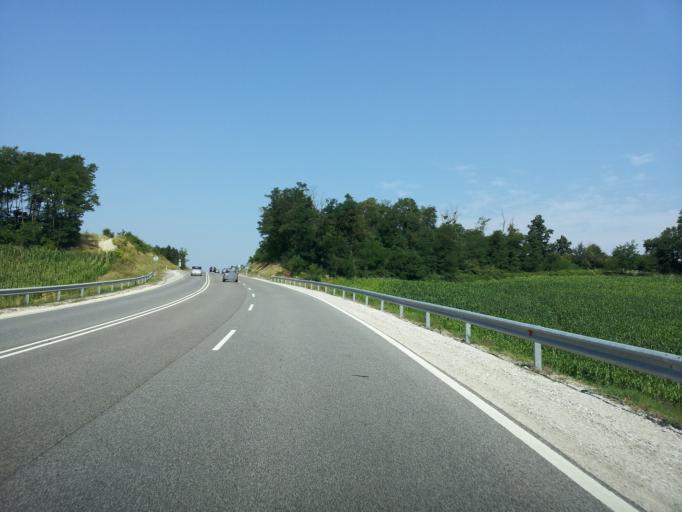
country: HU
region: Zala
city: Pacsa
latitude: 46.8289
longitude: 17.0519
